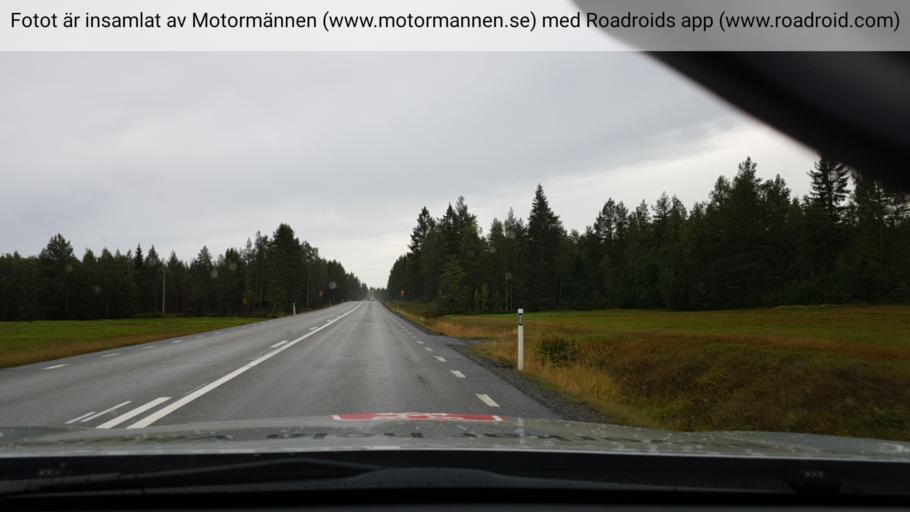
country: SE
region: Vaesterbotten
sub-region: Robertsfors Kommun
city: Robertsfors
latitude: 64.2097
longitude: 21.0179
